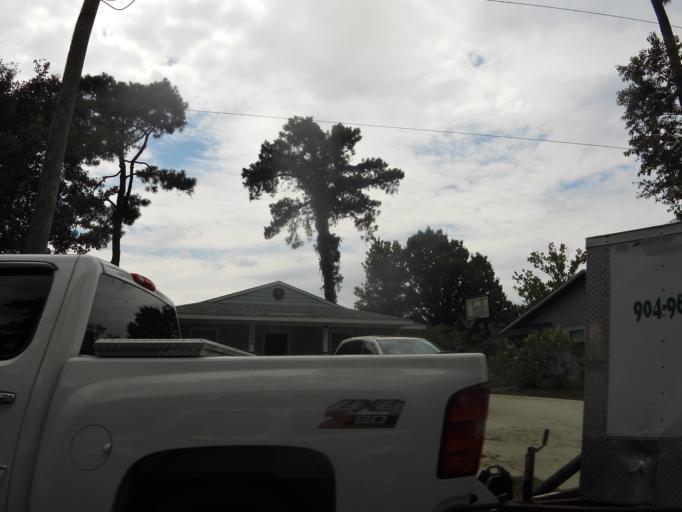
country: US
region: Florida
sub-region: Duval County
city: Atlantic Beach
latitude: 30.3302
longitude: -81.4197
